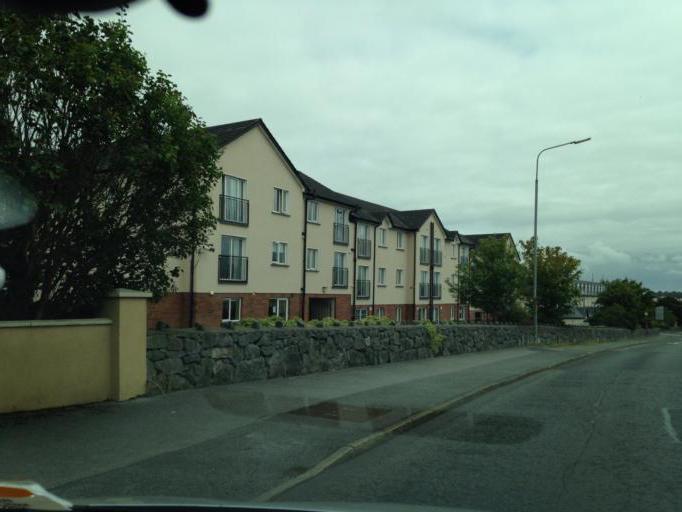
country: IE
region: Connaught
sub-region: County Galway
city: Gaillimh
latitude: 53.2886
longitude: -9.0492
